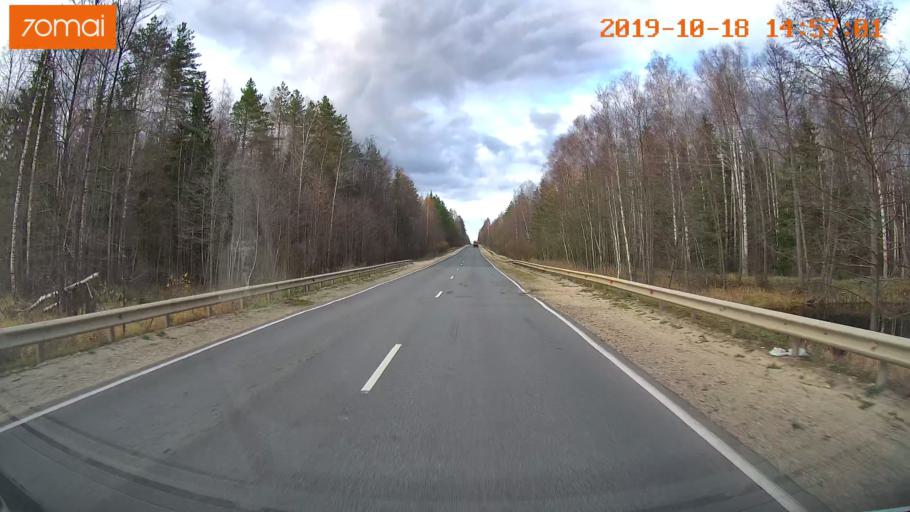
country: RU
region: Vladimir
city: Kurlovo
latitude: 55.4734
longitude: 40.5837
